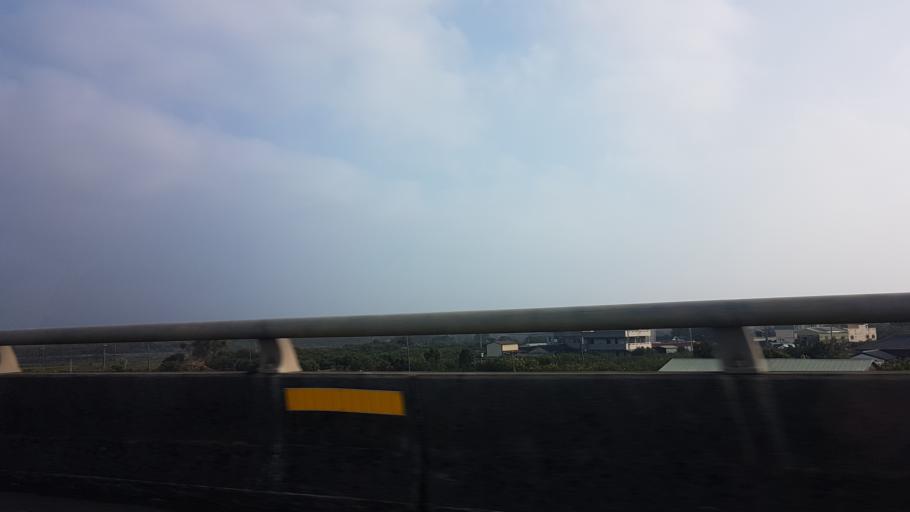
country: TW
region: Taiwan
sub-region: Chiayi
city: Taibao
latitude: 23.4168
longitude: 120.3991
